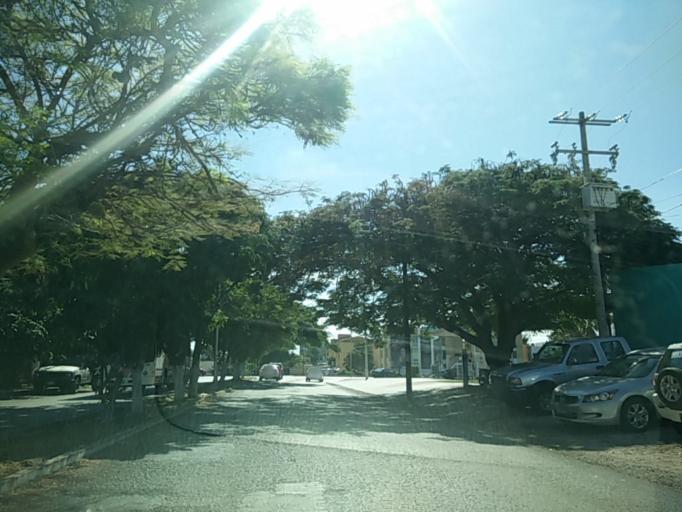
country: MX
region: Yucatan
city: Merida
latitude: 20.9979
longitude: -89.6060
